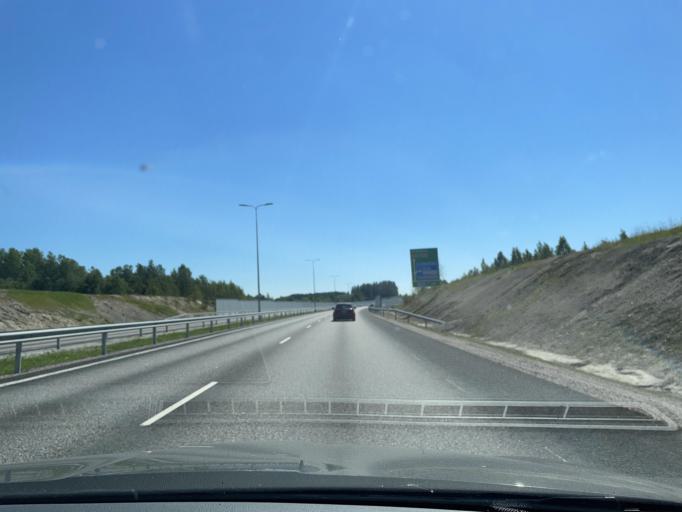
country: FI
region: Central Finland
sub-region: AEaenekoski
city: AEaenekoski
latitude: 62.4267
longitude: 25.6927
